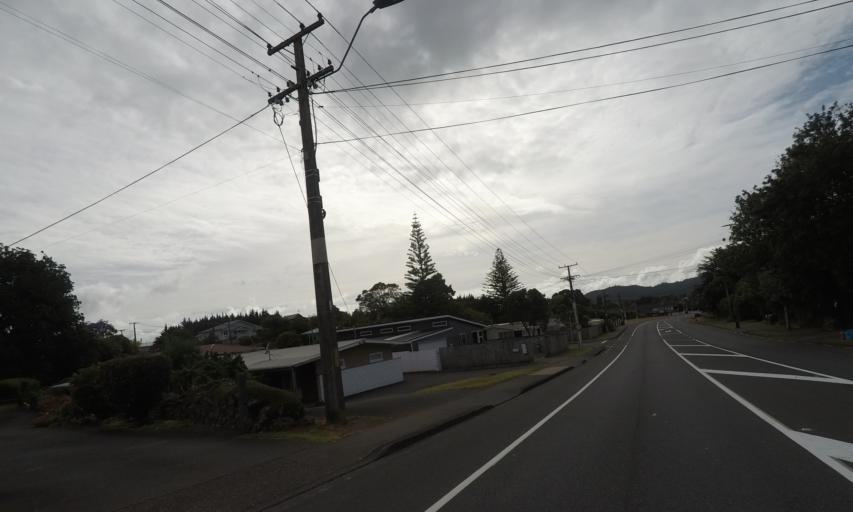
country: NZ
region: Northland
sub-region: Whangarei
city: Whangarei
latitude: -35.6918
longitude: 174.3087
